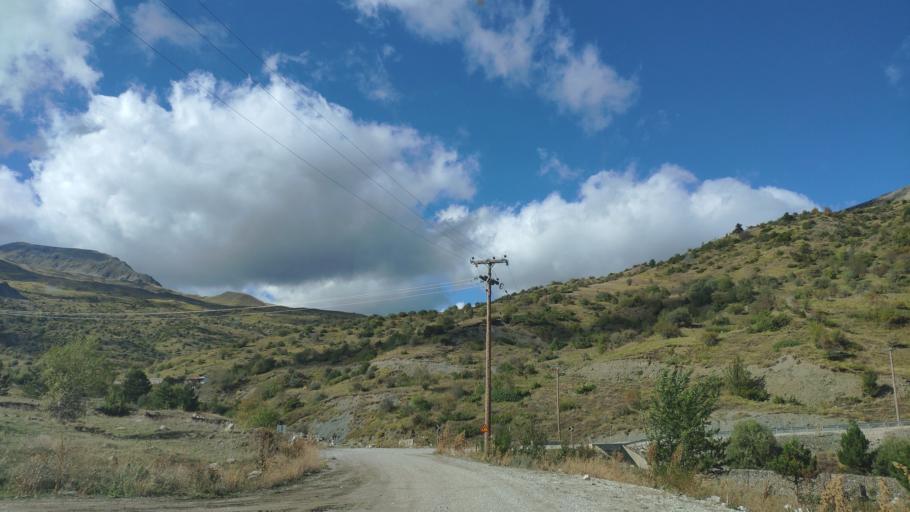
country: AL
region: Korce
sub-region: Rrethi i Devollit
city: Miras
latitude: 40.3957
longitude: 20.8369
